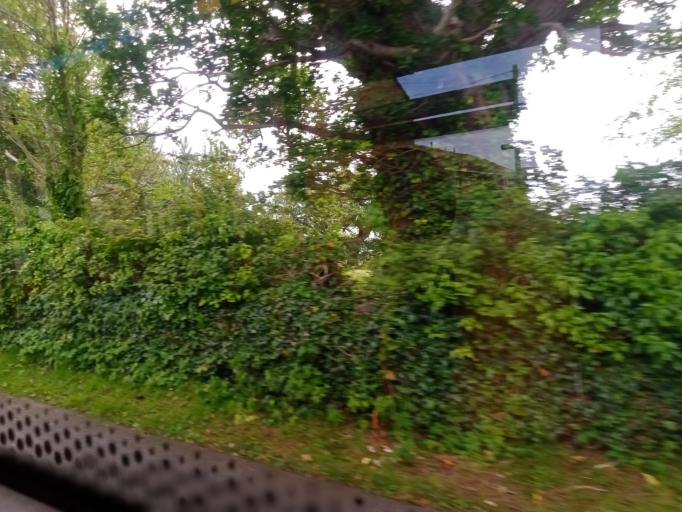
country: GB
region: Wales
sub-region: Anglesey
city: Llangoed
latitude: 53.2778
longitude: -4.0928
